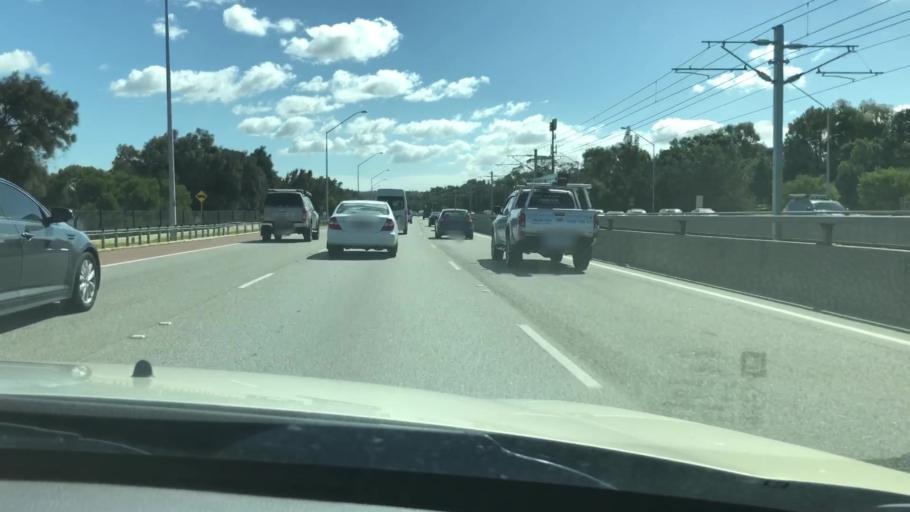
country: AU
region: Western Australia
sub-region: South Perth
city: Como
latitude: -31.9878
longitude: 115.8530
